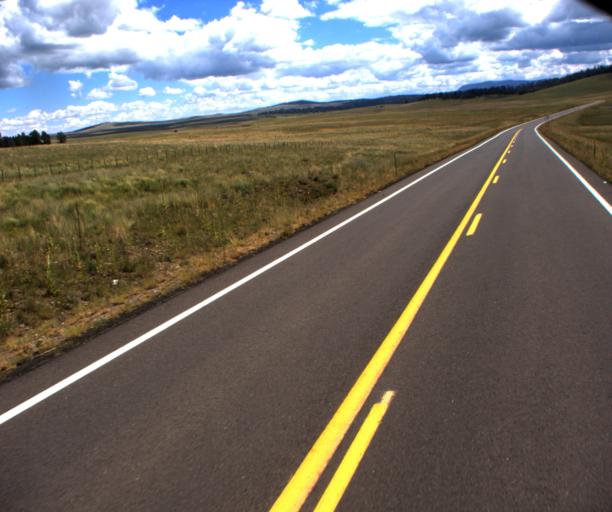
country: US
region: Arizona
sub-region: Apache County
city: Eagar
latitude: 33.9206
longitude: -109.4448
